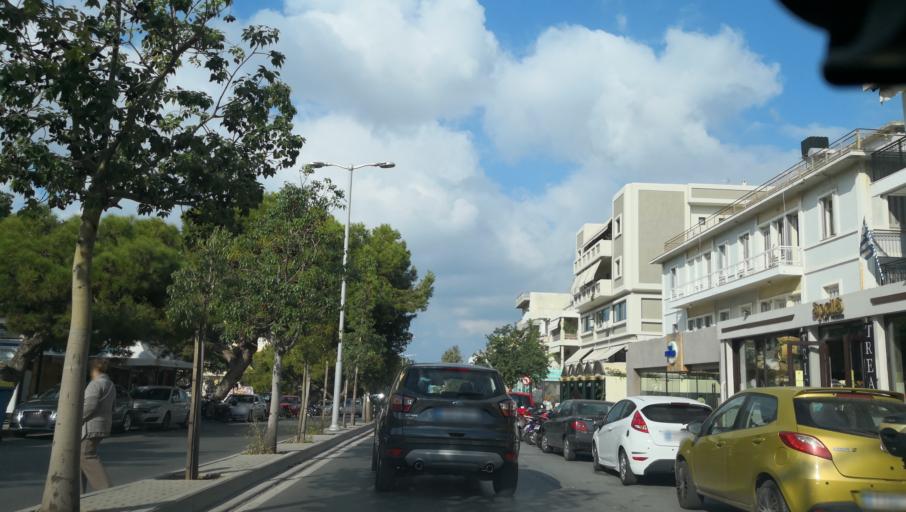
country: GR
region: Crete
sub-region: Nomos Irakleiou
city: Irakleion
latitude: 35.3328
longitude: 25.1385
